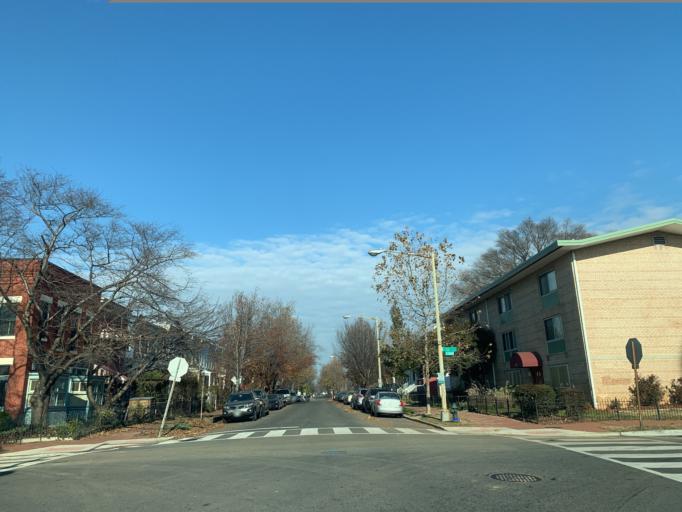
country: US
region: Washington, D.C.
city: Washington, D.C.
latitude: 38.8839
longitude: -76.9882
